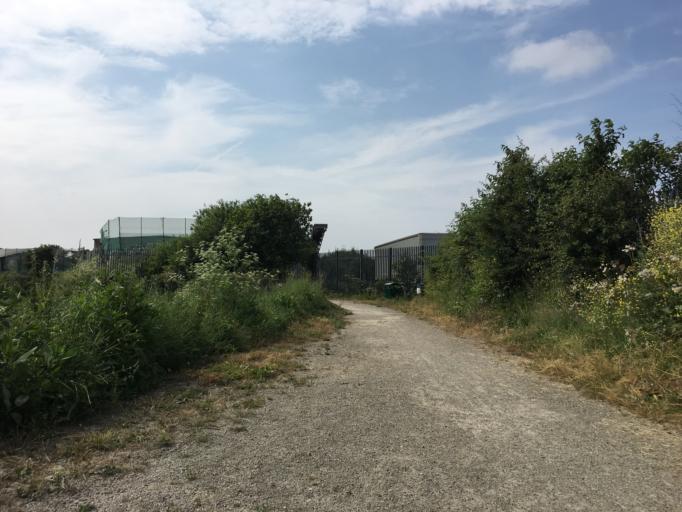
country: GB
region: England
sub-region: Kent
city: Sittingbourne
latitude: 51.3470
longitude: 0.7399
